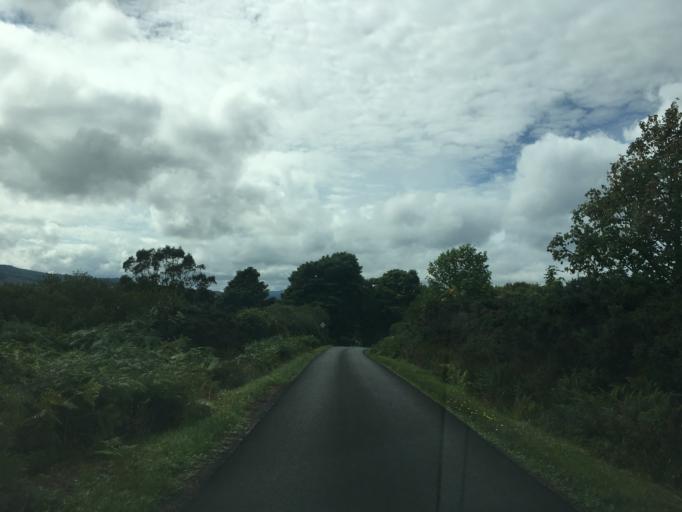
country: GB
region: Scotland
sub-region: Argyll and Bute
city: Tarbert
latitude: 55.8718
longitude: -5.3005
